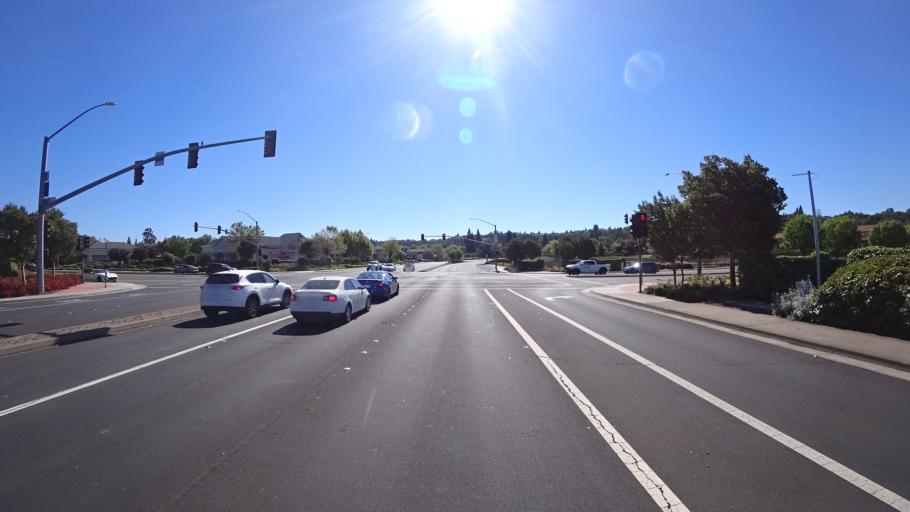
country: US
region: California
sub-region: Placer County
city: Rocklin
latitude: 38.8145
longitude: -121.2584
